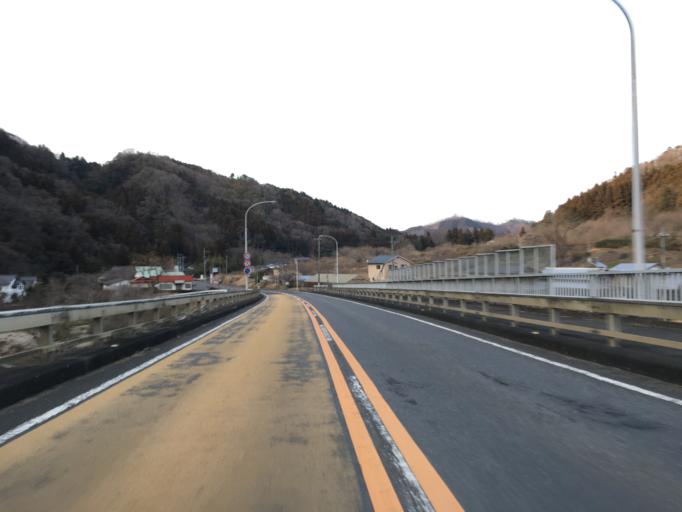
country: JP
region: Ibaraki
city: Daigo
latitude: 36.8282
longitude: 140.3791
